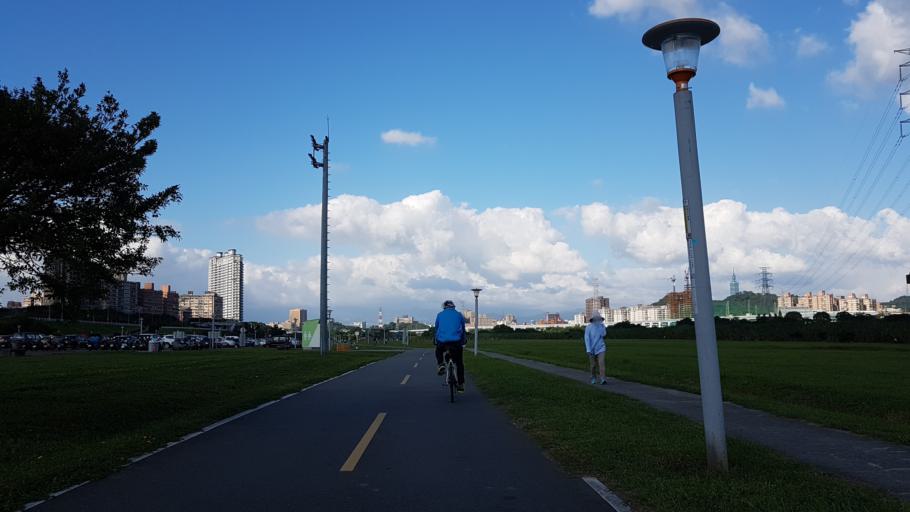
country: TW
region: Taipei
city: Taipei
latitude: 24.9915
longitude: 121.5288
